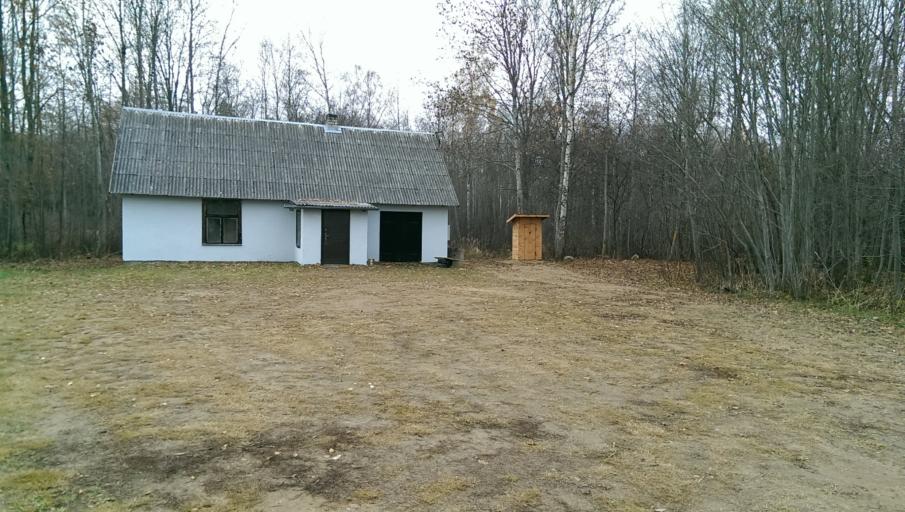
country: LV
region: Kuldigas Rajons
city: Kuldiga
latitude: 56.8387
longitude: 21.9383
